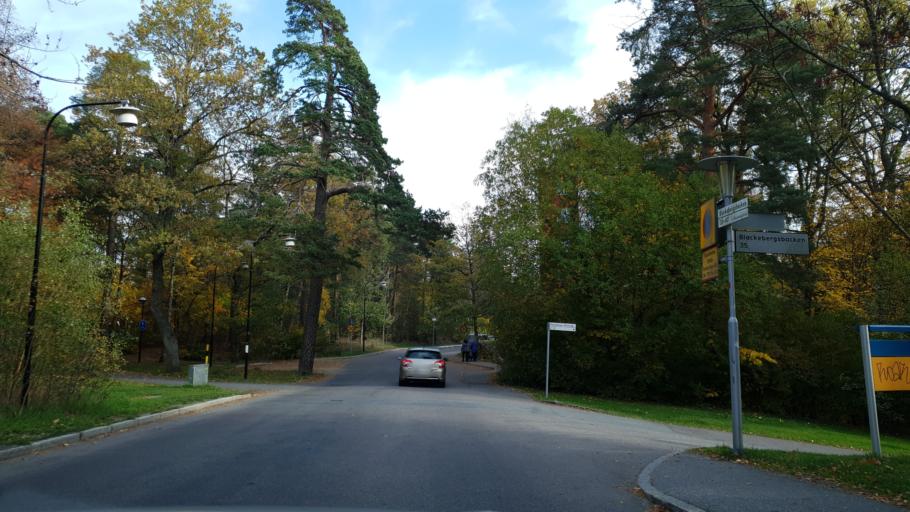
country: SE
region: Stockholm
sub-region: Stockholms Kommun
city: Bromma
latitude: 59.3412
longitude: 17.8825
